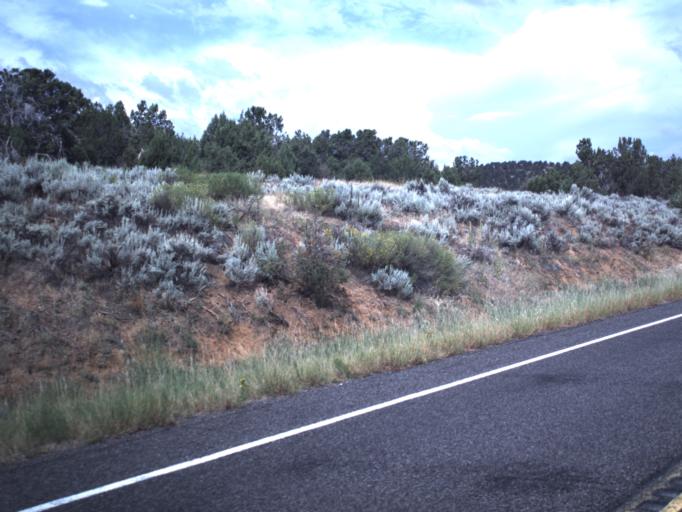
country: US
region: Utah
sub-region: Kane County
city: Kanab
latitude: 37.2519
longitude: -112.7616
